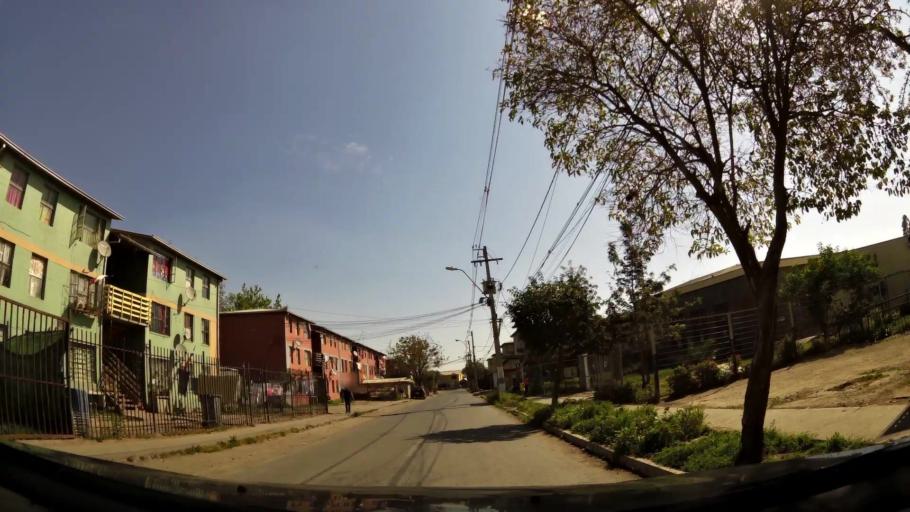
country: CL
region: Santiago Metropolitan
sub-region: Provincia de Santiago
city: La Pintana
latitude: -33.6330
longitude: -70.6230
